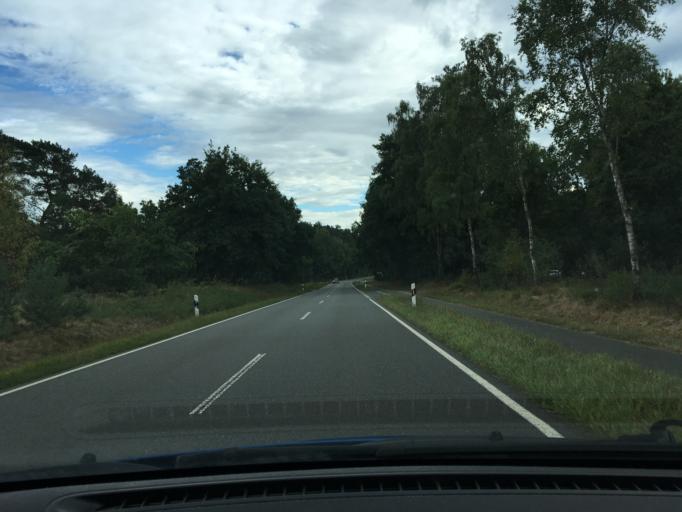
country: DE
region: Lower Saxony
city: Undeloh
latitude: 53.2385
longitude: 9.9187
